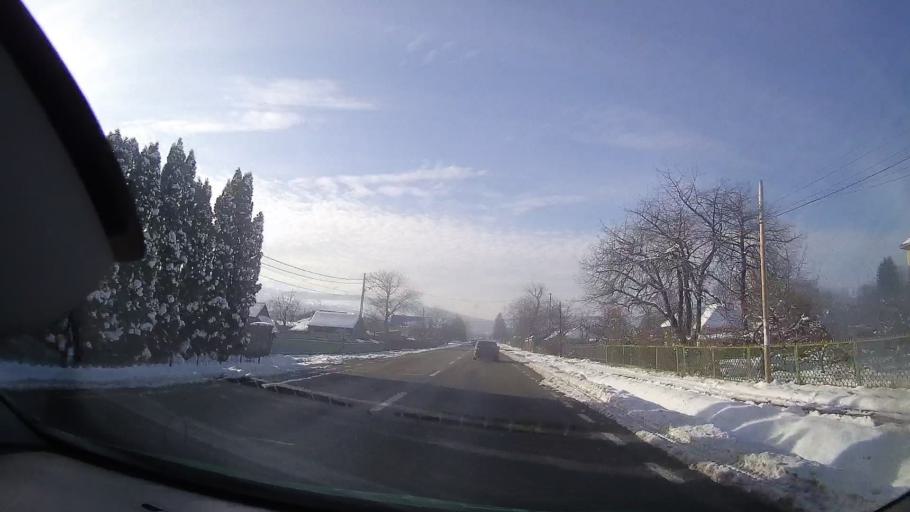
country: RO
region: Neamt
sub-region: Comuna Dobreni
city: Dobreni
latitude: 46.9962
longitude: 26.3990
